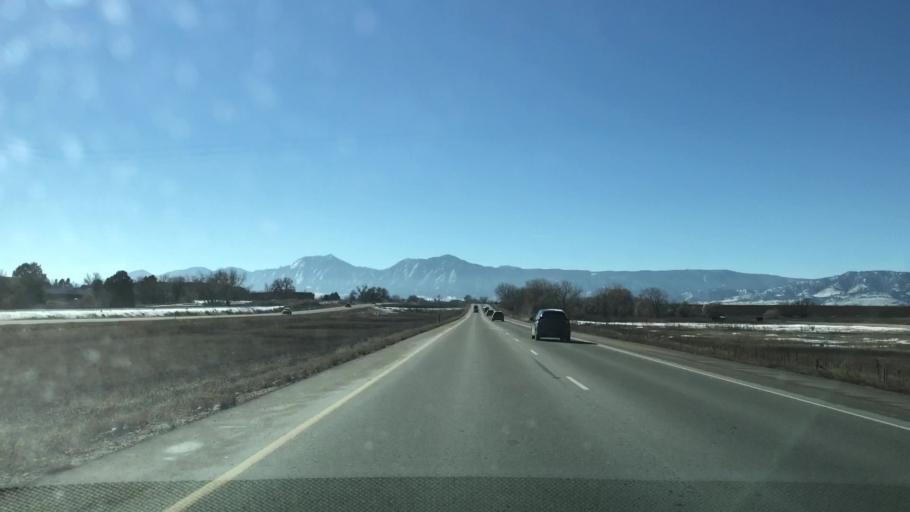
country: US
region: Colorado
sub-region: Boulder County
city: Gunbarrel
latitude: 40.0716
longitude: -105.2107
